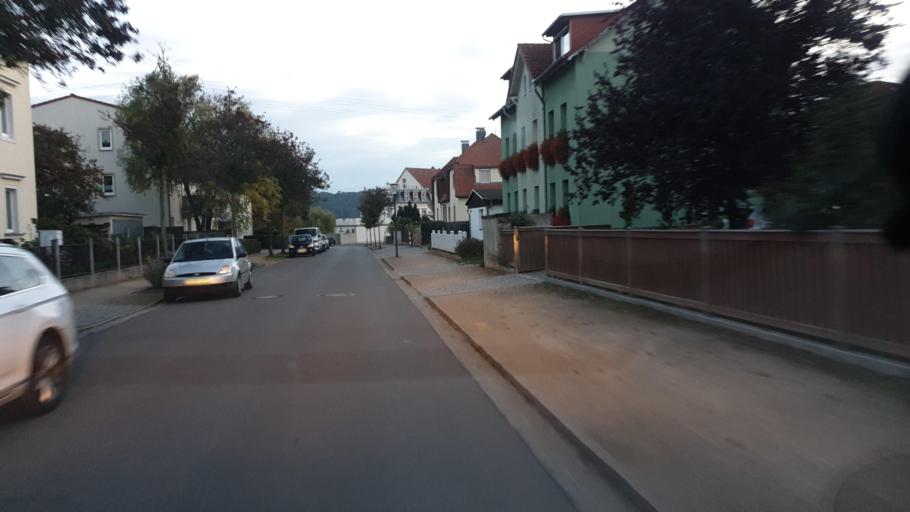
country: DE
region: Saxony
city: Radebeul
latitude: 51.1048
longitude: 13.6229
